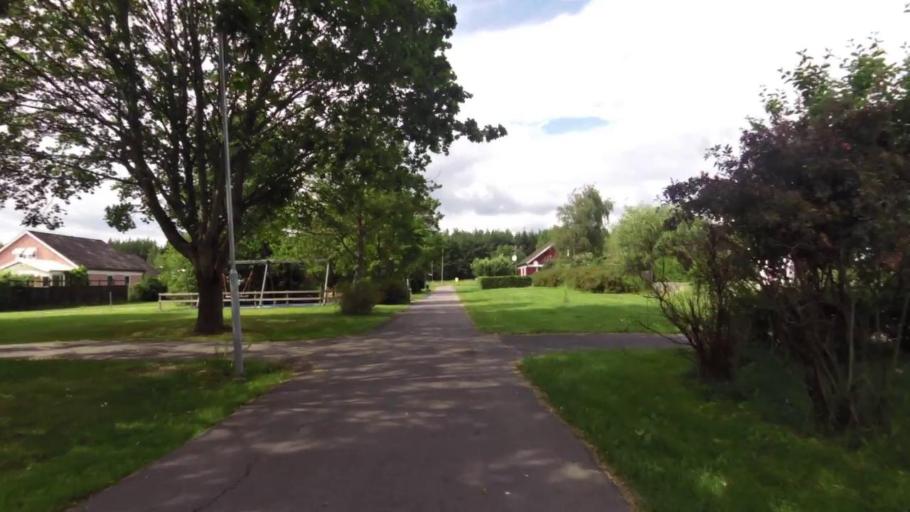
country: SE
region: OEstergoetland
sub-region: Linkopings Kommun
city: Malmslatt
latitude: 58.4181
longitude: 15.5614
